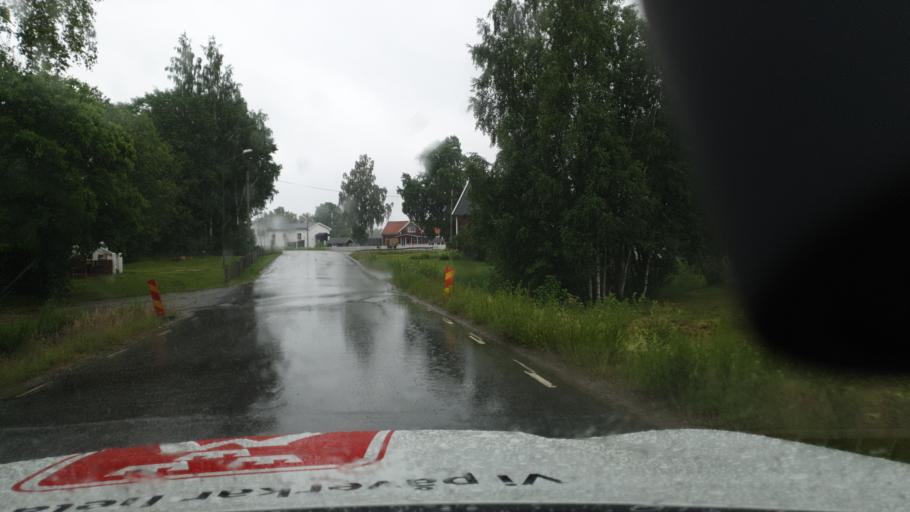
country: SE
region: Vaesterbotten
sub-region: Nordmalings Kommun
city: Nordmaling
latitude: 63.5476
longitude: 19.3918
